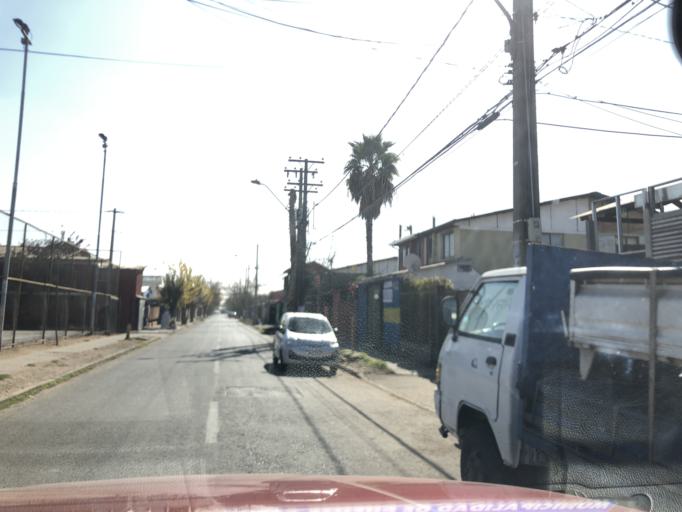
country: CL
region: Santiago Metropolitan
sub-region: Provincia de Cordillera
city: Puente Alto
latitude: -33.5660
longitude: -70.5715
